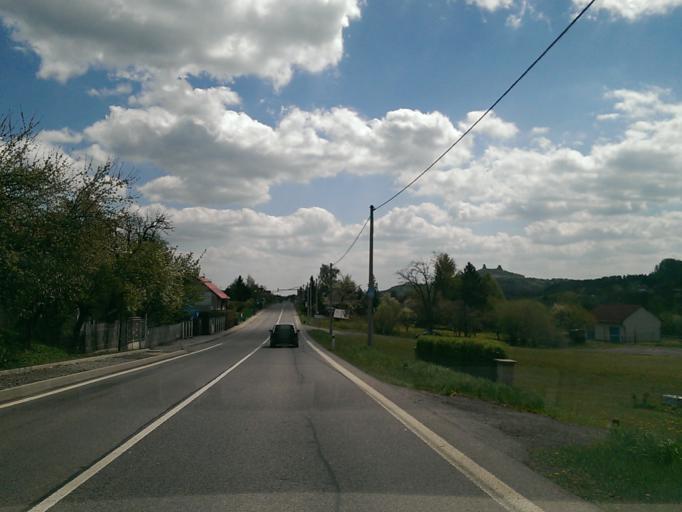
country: CZ
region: Liberecky
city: Rovensko pod Troskami
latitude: 50.5531
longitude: 15.2115
